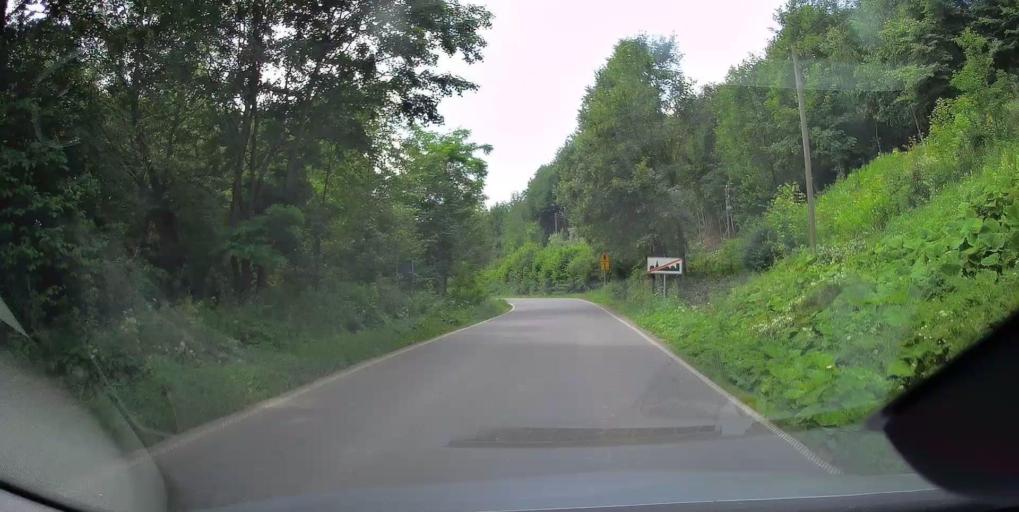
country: PL
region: Lesser Poland Voivodeship
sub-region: Powiat nowosadecki
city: Korzenna
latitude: 49.7303
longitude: 20.7729
